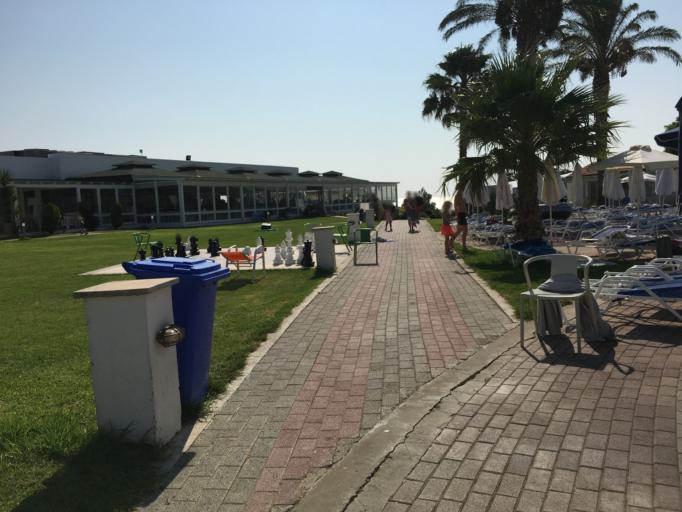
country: GR
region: South Aegean
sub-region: Nomos Dodekanisou
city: Rodos
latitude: 36.4058
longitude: 28.2265
